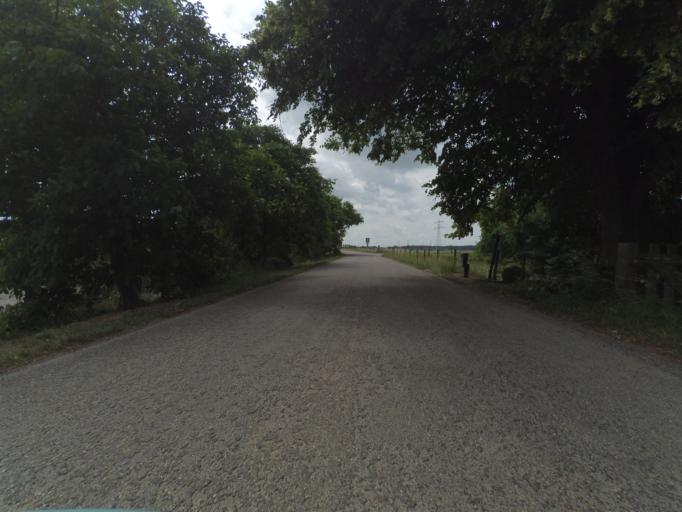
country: NL
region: Zeeland
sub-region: Gemeente Borsele
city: Borssele
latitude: 51.4817
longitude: 3.7414
